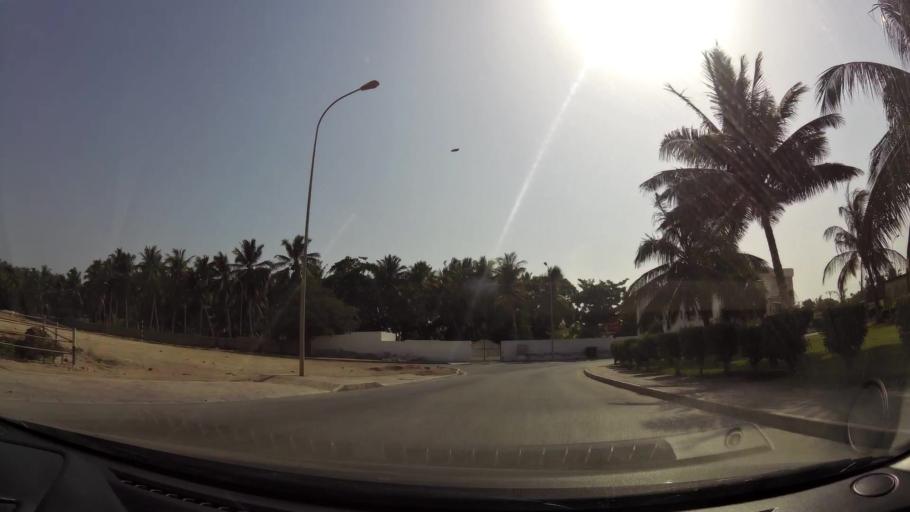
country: OM
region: Zufar
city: Salalah
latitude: 17.0036
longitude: 54.0584
